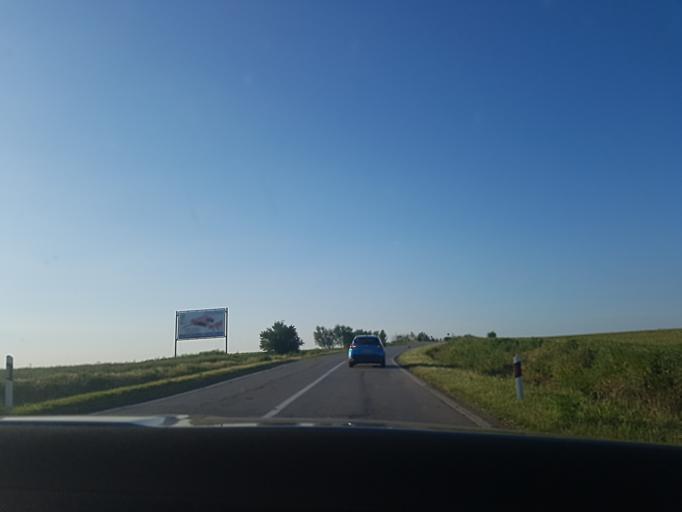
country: RS
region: Autonomna Pokrajina Vojvodina
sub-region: Juznobanatski Okrug
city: Vrsac
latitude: 45.1590
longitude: 21.2902
